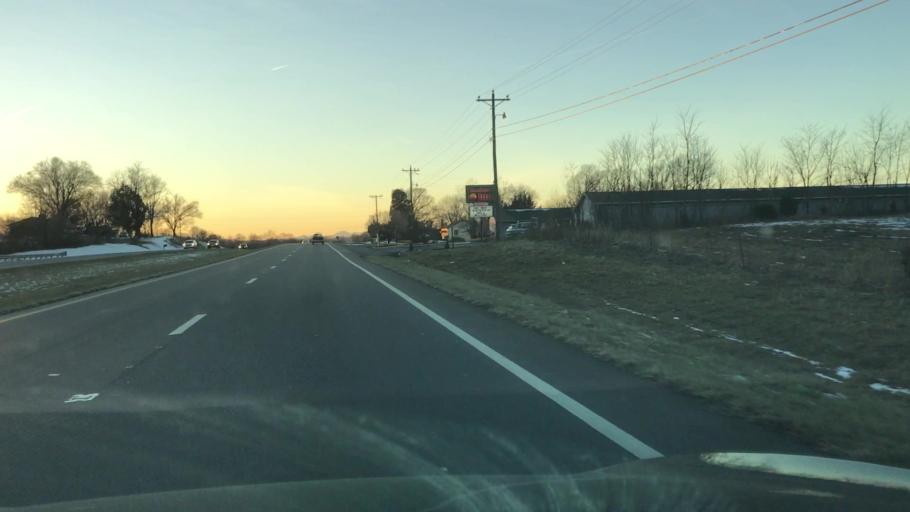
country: US
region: Virginia
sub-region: Bedford County
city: Forest
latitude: 37.3006
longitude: -79.3682
